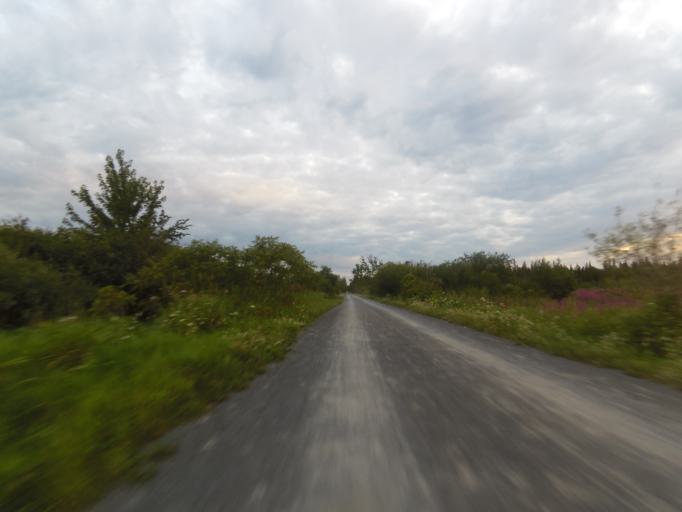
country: CA
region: Ontario
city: Bells Corners
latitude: 45.2466
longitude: -75.9391
